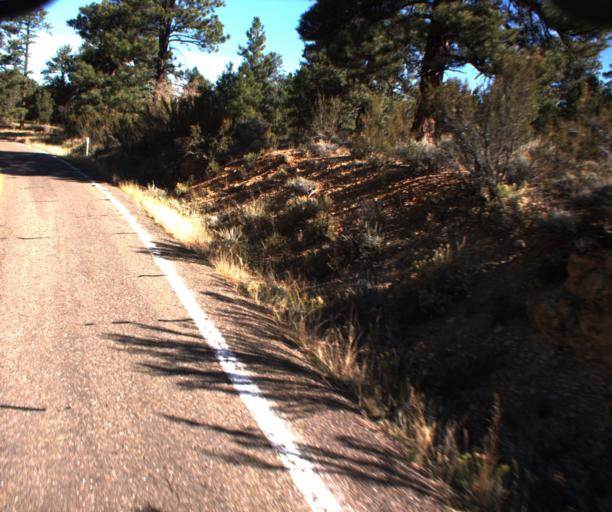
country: US
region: Arizona
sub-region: Coconino County
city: Fredonia
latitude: 36.7801
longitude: -112.2564
